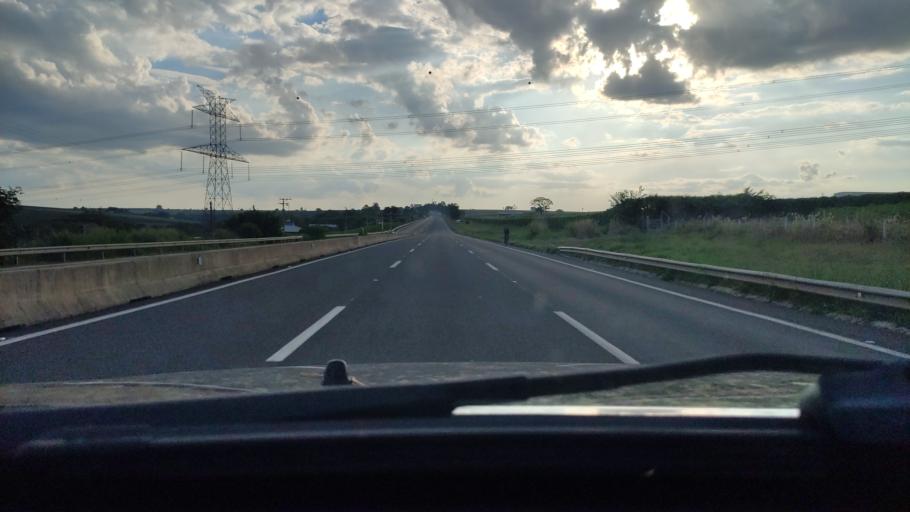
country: BR
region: Sao Paulo
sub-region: Mogi-Mirim
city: Mogi Mirim
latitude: -22.4503
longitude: -47.0646
